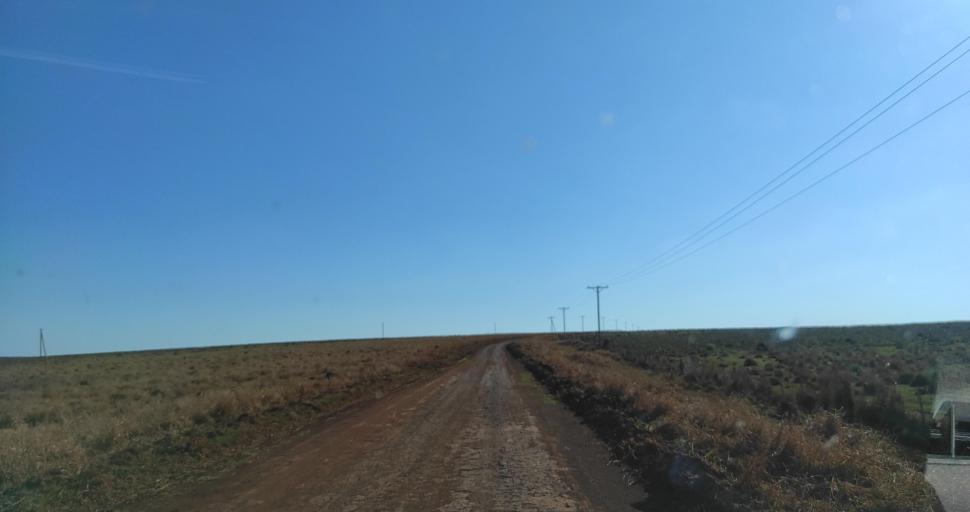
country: PY
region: Itapua
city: San Juan del Parana
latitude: -27.4363
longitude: -56.0652
